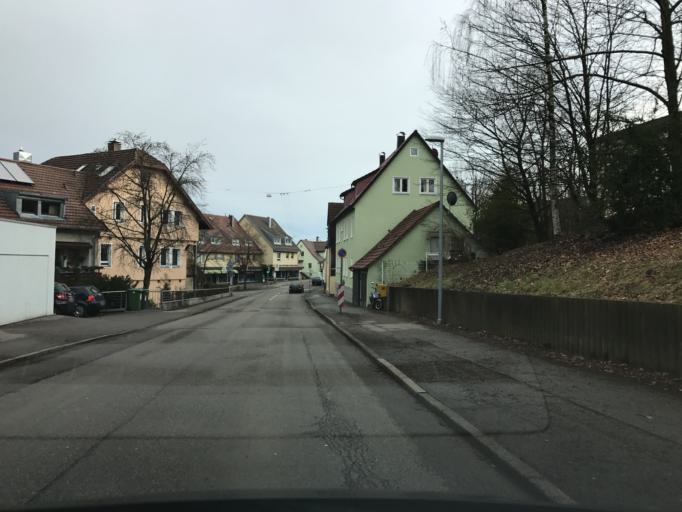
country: DE
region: Baden-Wuerttemberg
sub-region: Regierungsbezirk Stuttgart
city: Ostfildern
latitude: 48.7242
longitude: 9.2060
